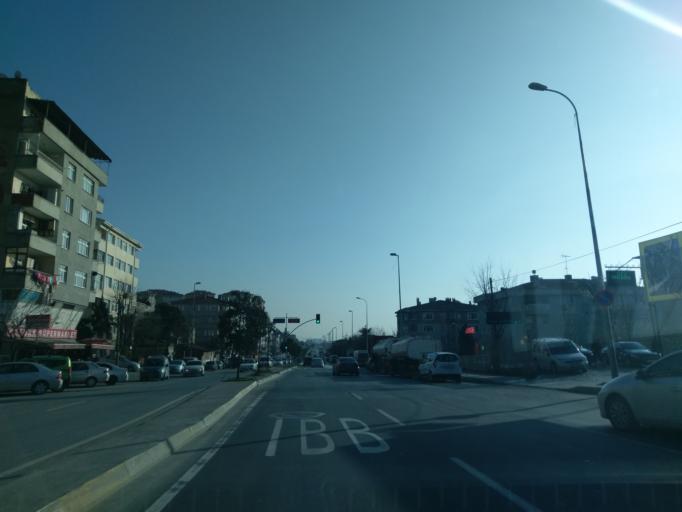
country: TR
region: Istanbul
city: Mahmutbey
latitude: 41.0321
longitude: 28.7682
